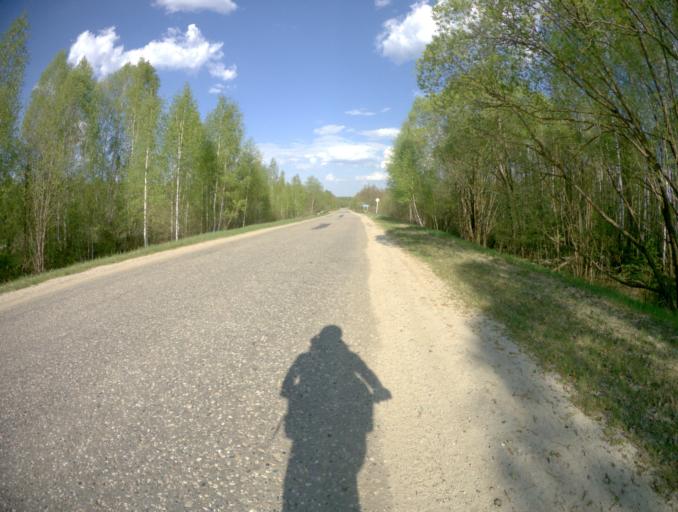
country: RU
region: Ivanovo
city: Kolobovo
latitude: 56.5475
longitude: 41.4787
